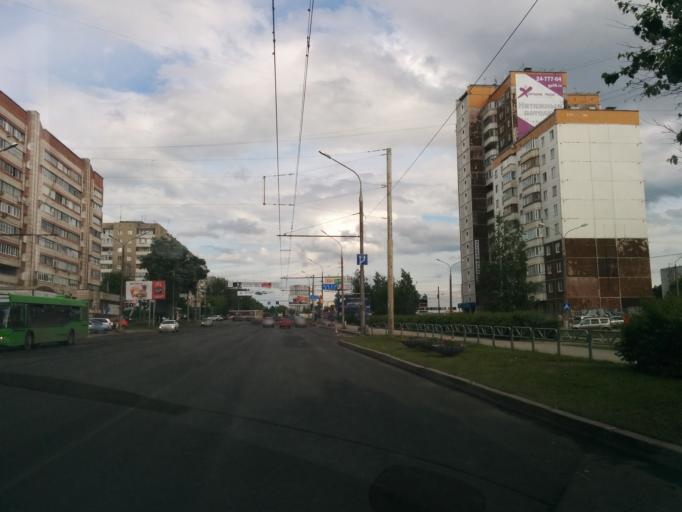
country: RU
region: Perm
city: Kondratovo
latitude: 57.9981
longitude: 56.1644
